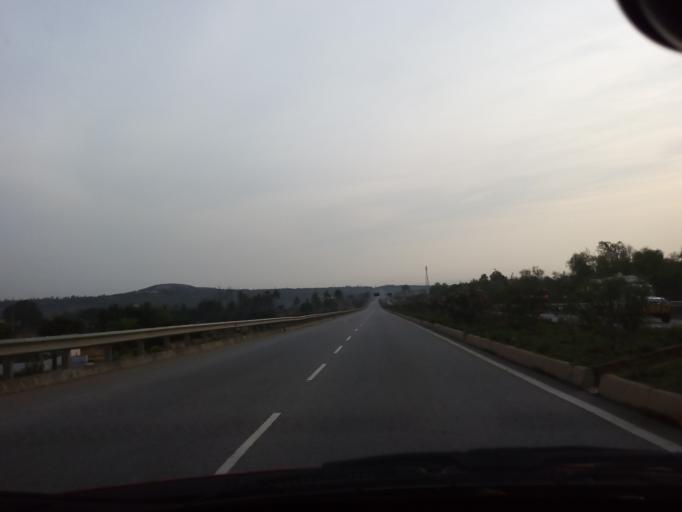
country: IN
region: Karnataka
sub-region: Chikkaballapur
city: Chik Ballapur
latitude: 13.5334
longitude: 77.7661
